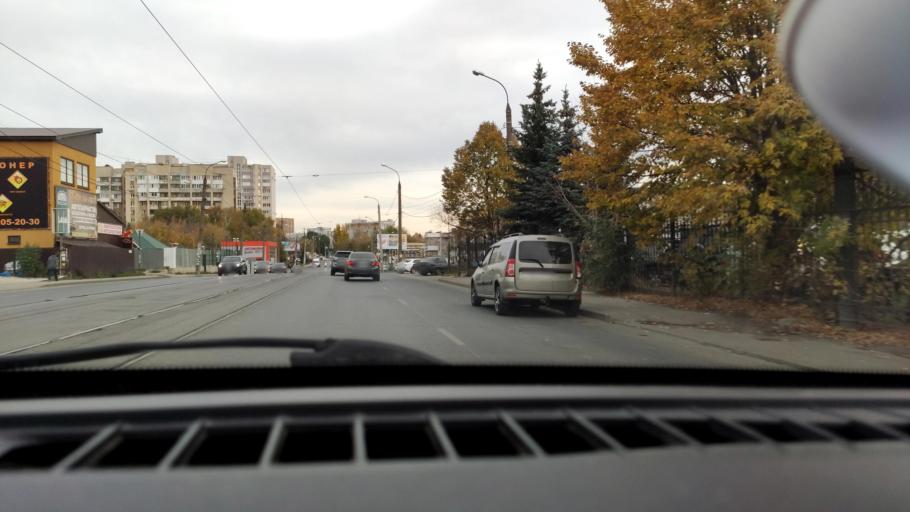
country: RU
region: Samara
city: Samara
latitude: 53.1936
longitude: 50.1644
